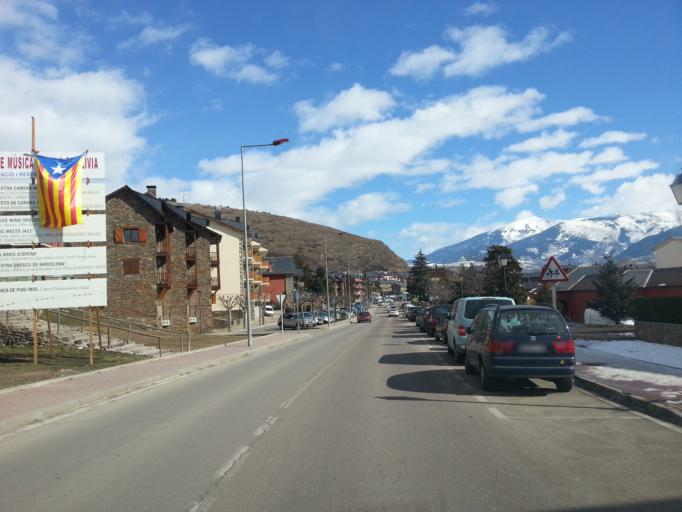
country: ES
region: Catalonia
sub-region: Provincia de Girona
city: Llivia
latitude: 42.4628
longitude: 1.9772
